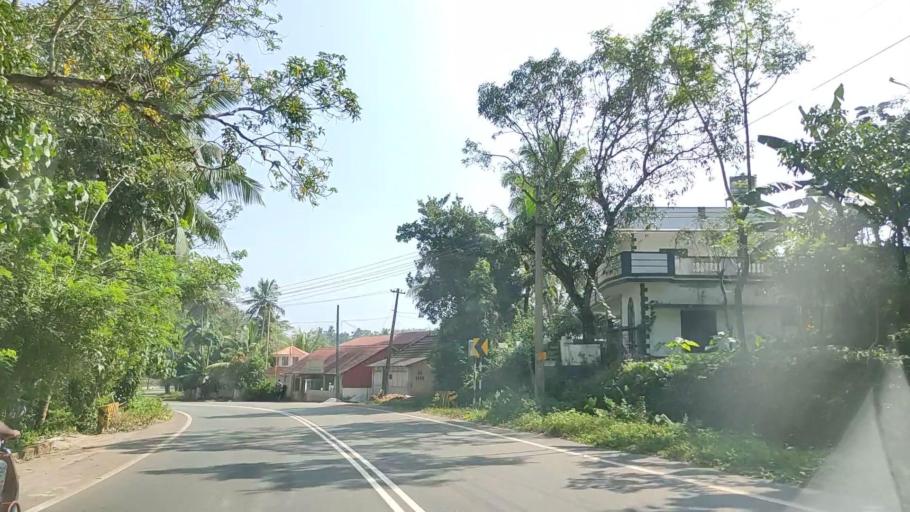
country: IN
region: Kerala
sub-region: Kollam
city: Punalur
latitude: 8.9316
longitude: 76.9972
